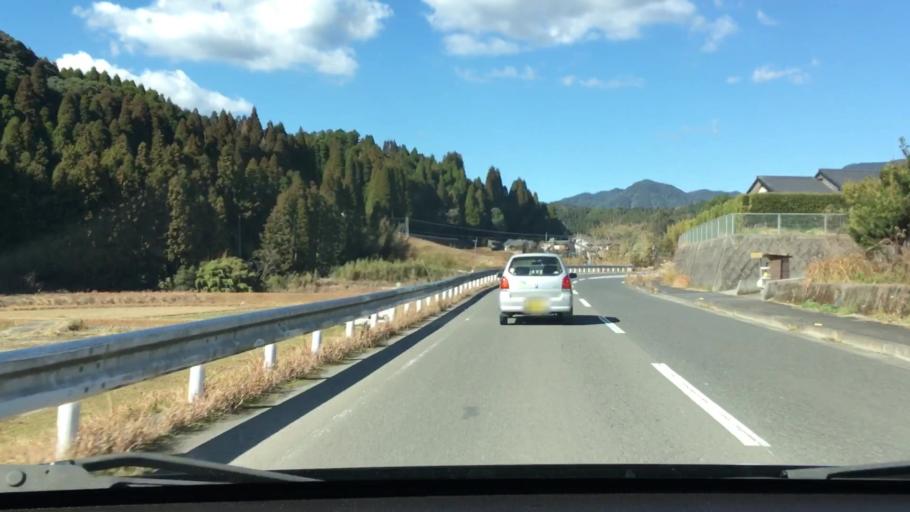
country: JP
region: Kagoshima
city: Ijuin
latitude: 31.6932
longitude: 130.4625
